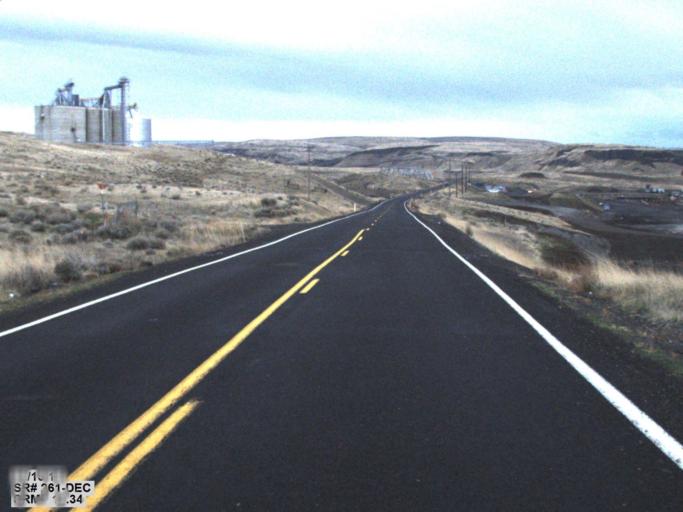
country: US
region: Washington
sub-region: Walla Walla County
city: Waitsburg
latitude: 46.5706
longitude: -118.2003
